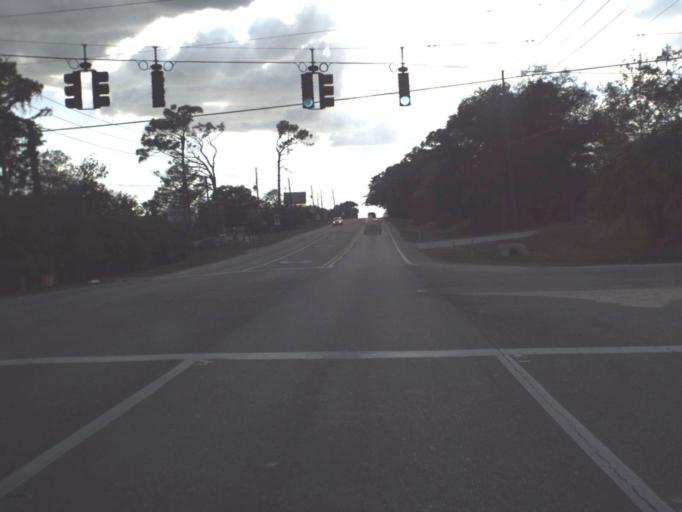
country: US
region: Florida
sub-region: Lake County
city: Mount Dora
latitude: 28.8007
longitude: -81.5925
